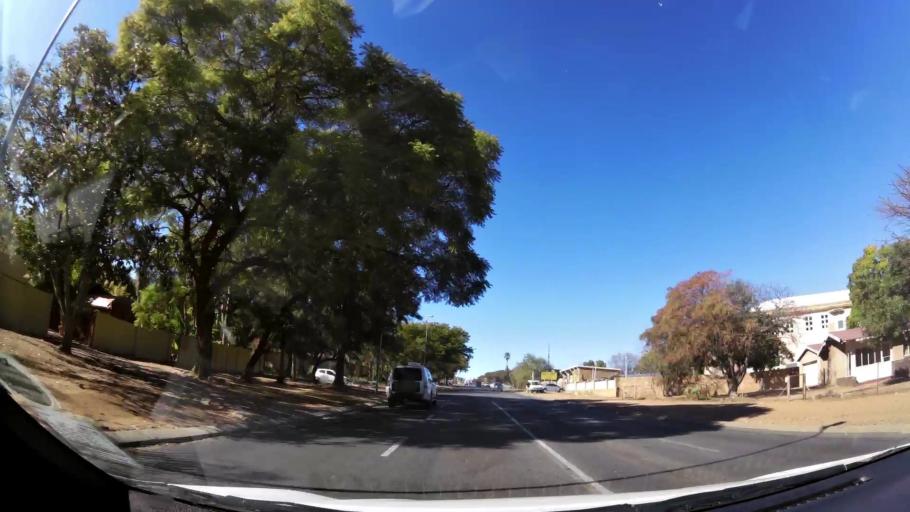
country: ZA
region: Limpopo
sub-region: Capricorn District Municipality
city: Polokwane
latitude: -23.8971
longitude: 29.4686
